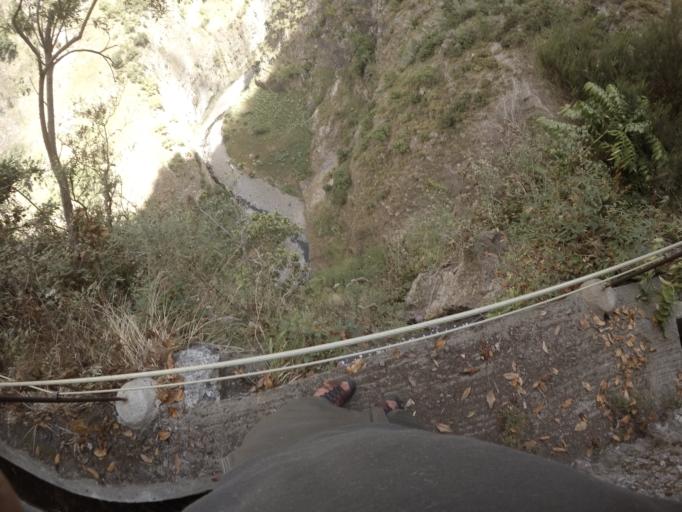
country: PT
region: Madeira
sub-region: Camara de Lobos
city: Curral das Freiras
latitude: 32.6940
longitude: -16.9617
